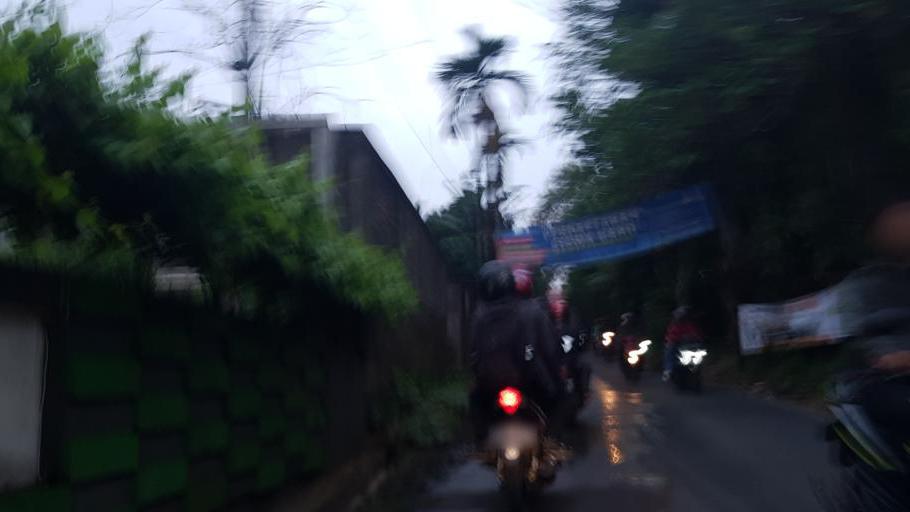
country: ID
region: West Java
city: Depok
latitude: -6.3670
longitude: 106.7967
